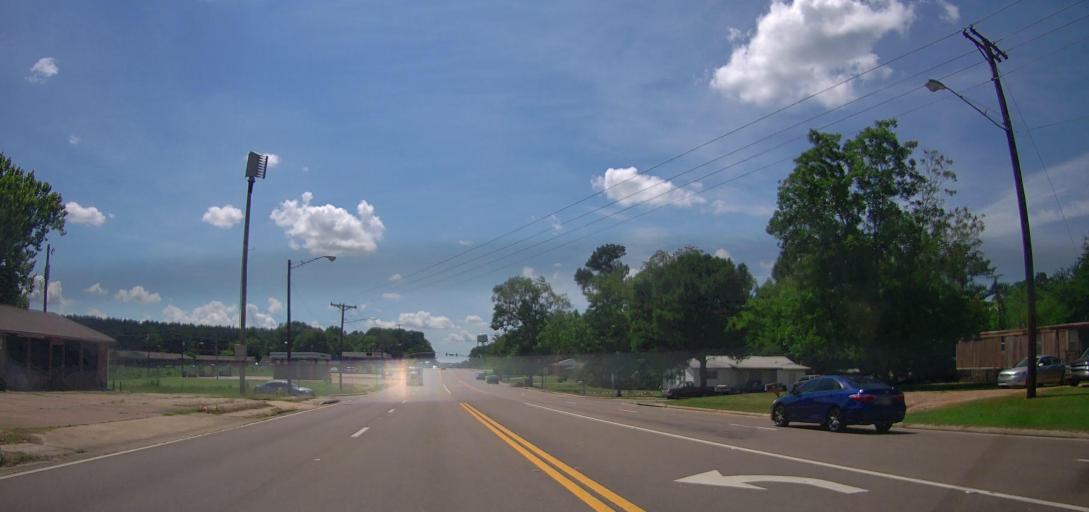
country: US
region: Mississippi
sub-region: Monroe County
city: Aberdeen
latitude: 33.8150
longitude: -88.5498
